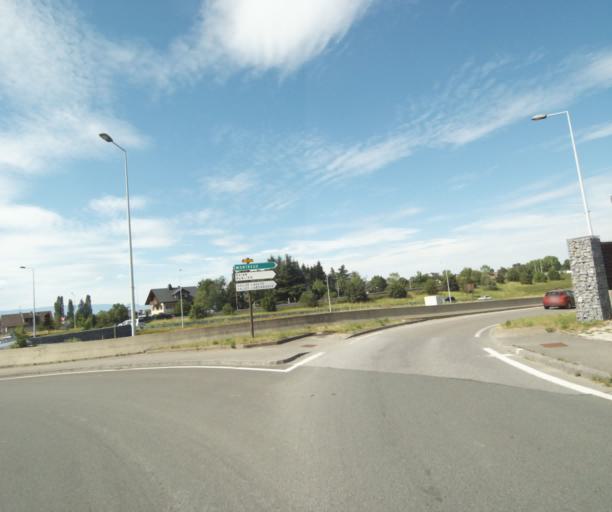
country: FR
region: Rhone-Alpes
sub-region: Departement de la Haute-Savoie
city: Thonon-les-Bains
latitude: 46.3527
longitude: 6.4775
